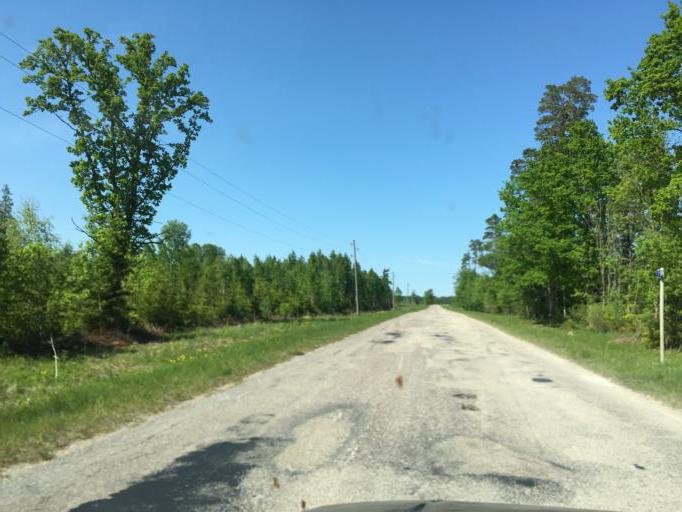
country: LV
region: Dundaga
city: Dundaga
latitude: 57.4593
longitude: 22.3218
